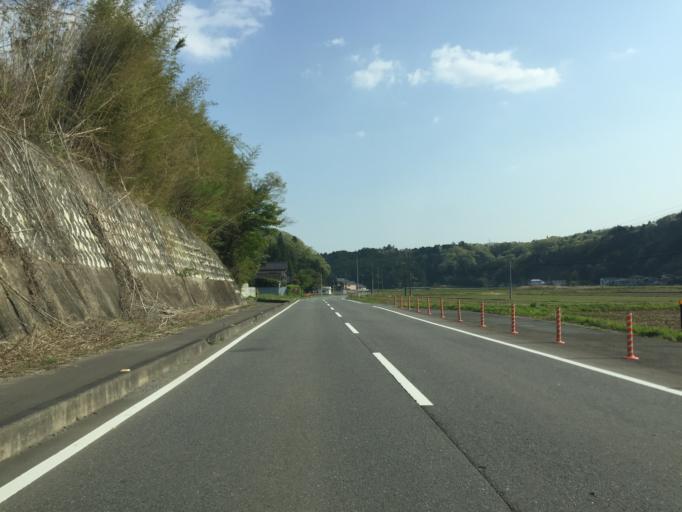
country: JP
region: Fukushima
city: Iwaki
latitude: 36.9753
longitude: 140.8017
